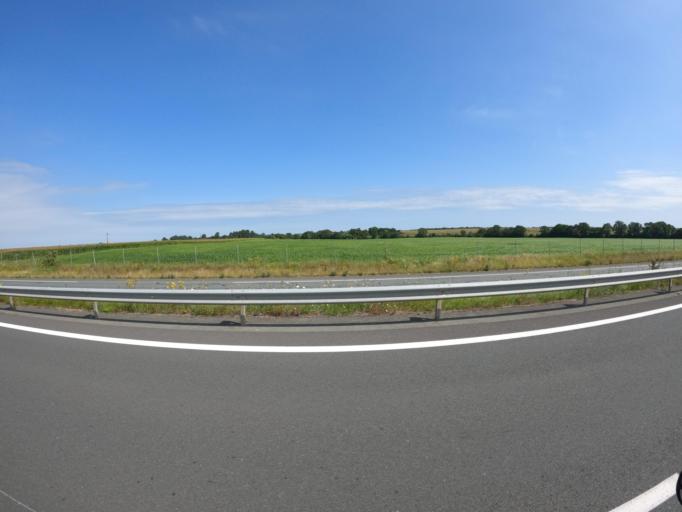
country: FR
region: Poitou-Charentes
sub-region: Departement des Deux-Sevres
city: Mauze-sur-le-Mignon
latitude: 46.2035
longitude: -0.7204
